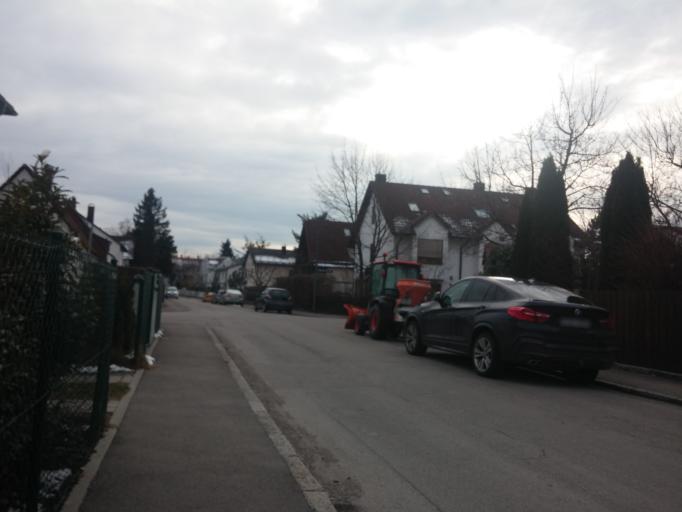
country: DE
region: Bavaria
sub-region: Upper Bavaria
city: Neubiberg
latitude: 48.1224
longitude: 11.6758
